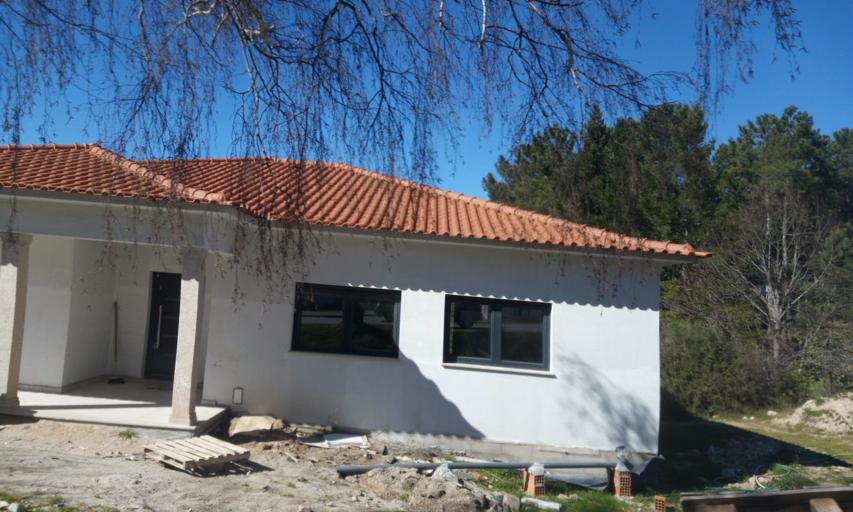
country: PT
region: Guarda
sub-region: Manteigas
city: Manteigas
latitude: 40.4747
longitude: -7.6011
